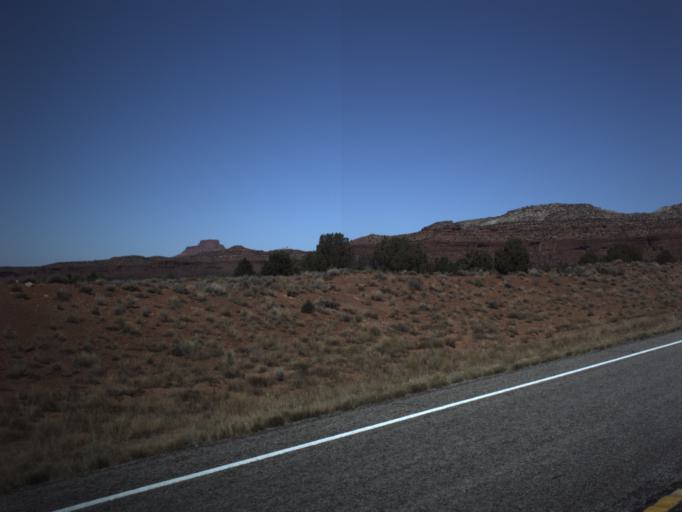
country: US
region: Utah
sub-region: San Juan County
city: Blanding
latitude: 37.6501
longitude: -110.1423
